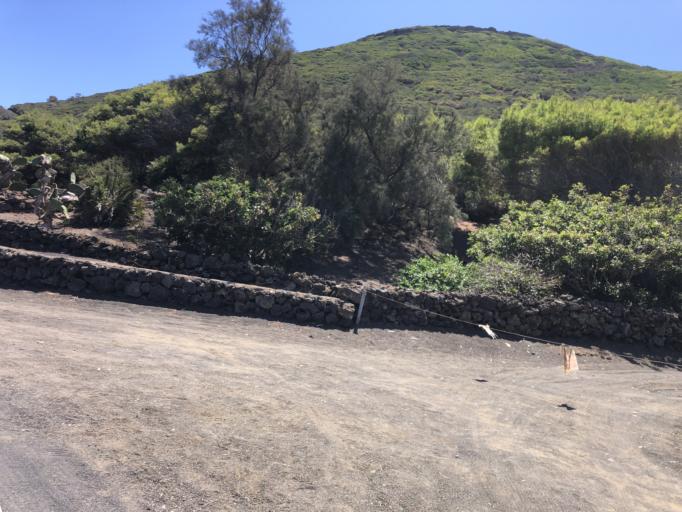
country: IT
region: Sicily
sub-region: Agrigento
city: Lampedusa
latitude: 35.8629
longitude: 12.8729
